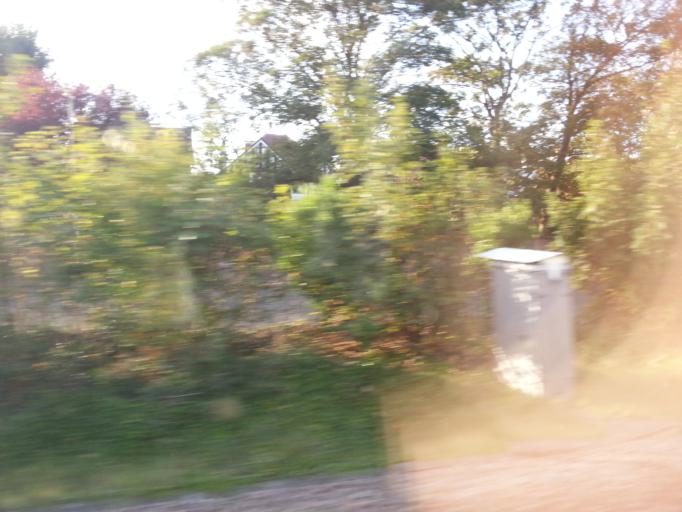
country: GB
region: England
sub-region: Sefton
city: Southport
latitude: 53.6049
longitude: -3.0400
